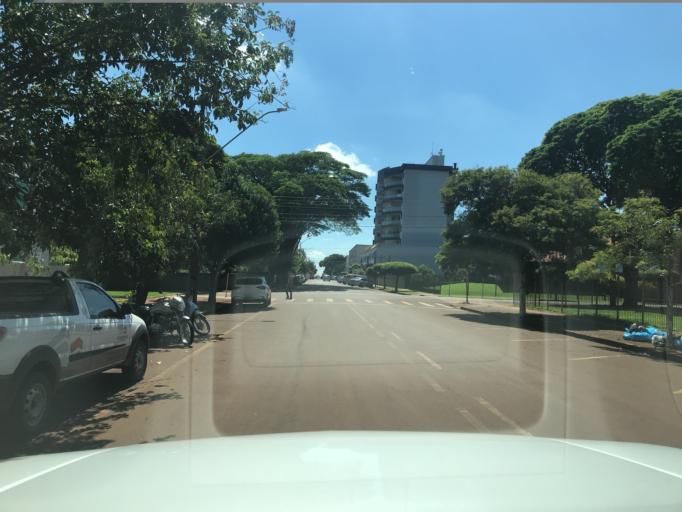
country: BR
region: Parana
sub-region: Palotina
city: Palotina
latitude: -24.2860
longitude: -53.8421
